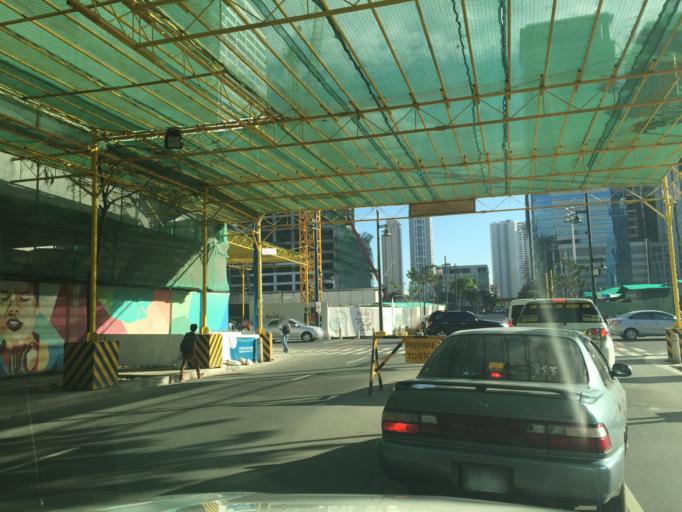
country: PH
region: Metro Manila
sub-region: Makati City
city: Makati City
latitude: 14.5551
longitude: 121.0529
